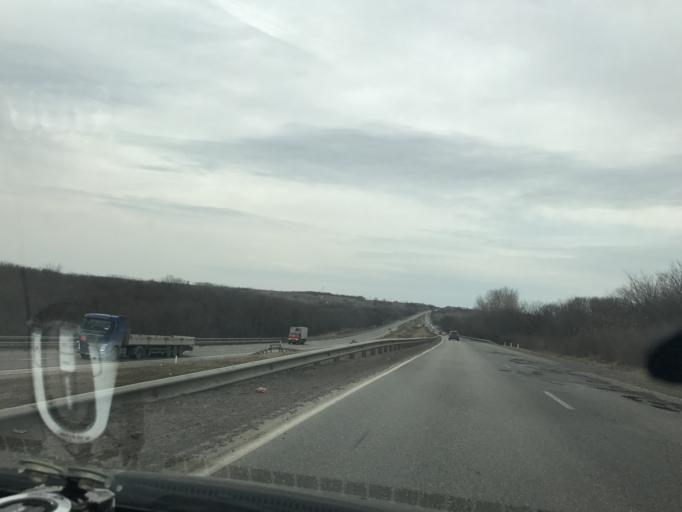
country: RU
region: Krasnodarskiy
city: Zavetnyy
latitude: 44.9117
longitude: 41.1606
